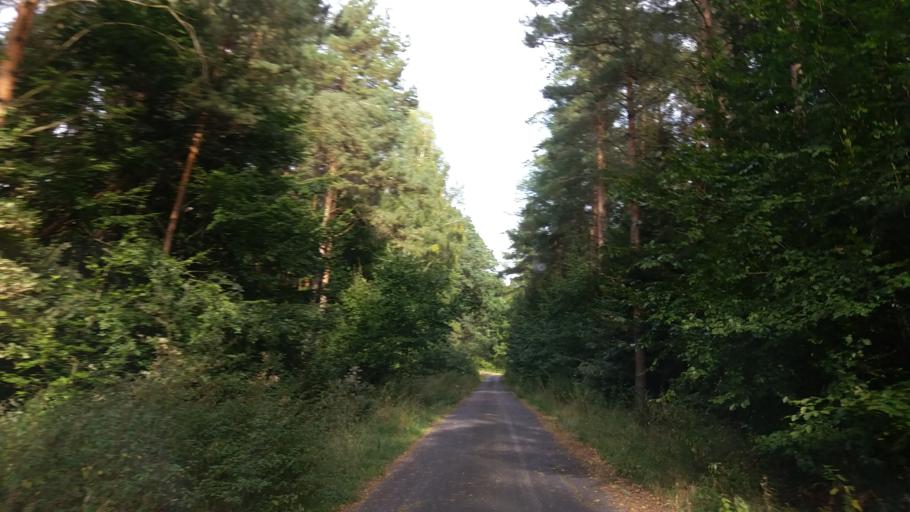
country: PL
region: West Pomeranian Voivodeship
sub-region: Powiat choszczenski
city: Krzecin
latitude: 52.9927
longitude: 15.4732
